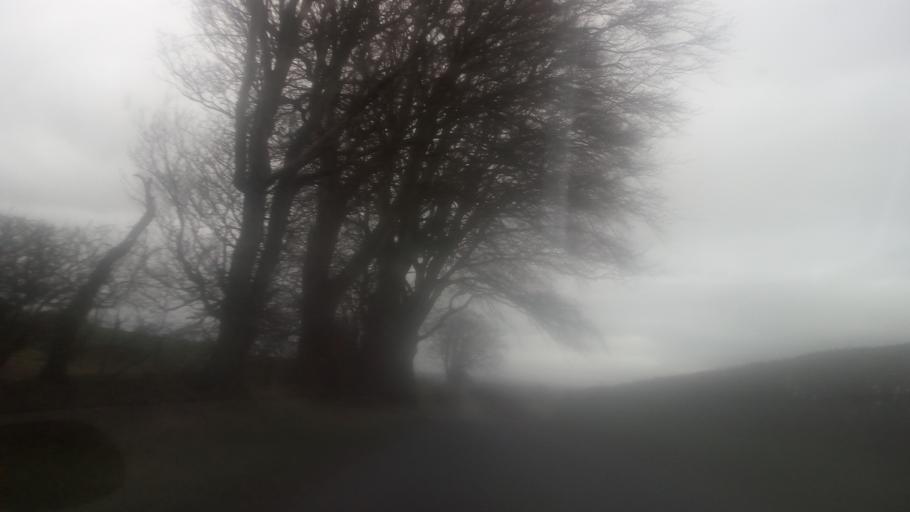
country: GB
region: Scotland
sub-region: The Scottish Borders
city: Jedburgh
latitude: 55.5009
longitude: -2.4795
